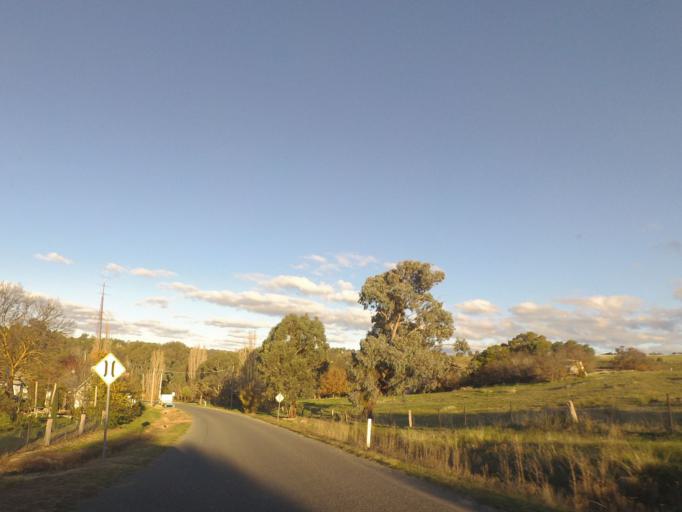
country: AU
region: Victoria
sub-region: Mount Alexander
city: Castlemaine
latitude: -37.1559
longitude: 144.2073
